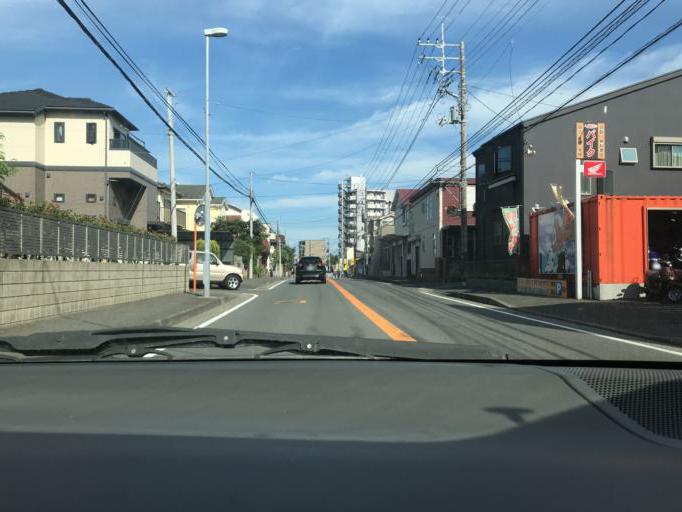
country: JP
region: Kanagawa
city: Fujisawa
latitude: 35.3413
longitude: 139.4599
